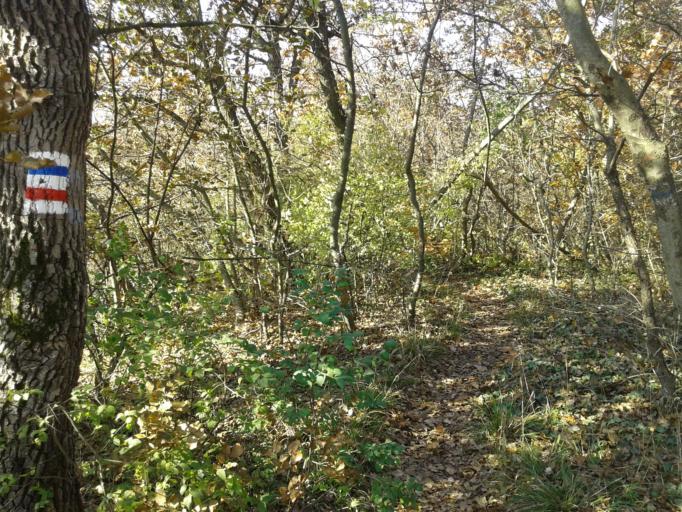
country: HU
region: Fejer
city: Bodajk
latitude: 47.3151
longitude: 18.2160
